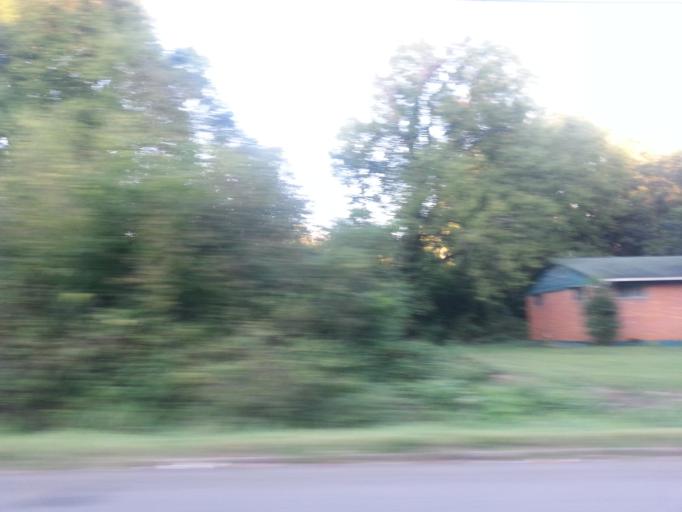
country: US
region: Tennessee
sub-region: Knox County
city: Knoxville
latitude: 35.9717
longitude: -83.8921
